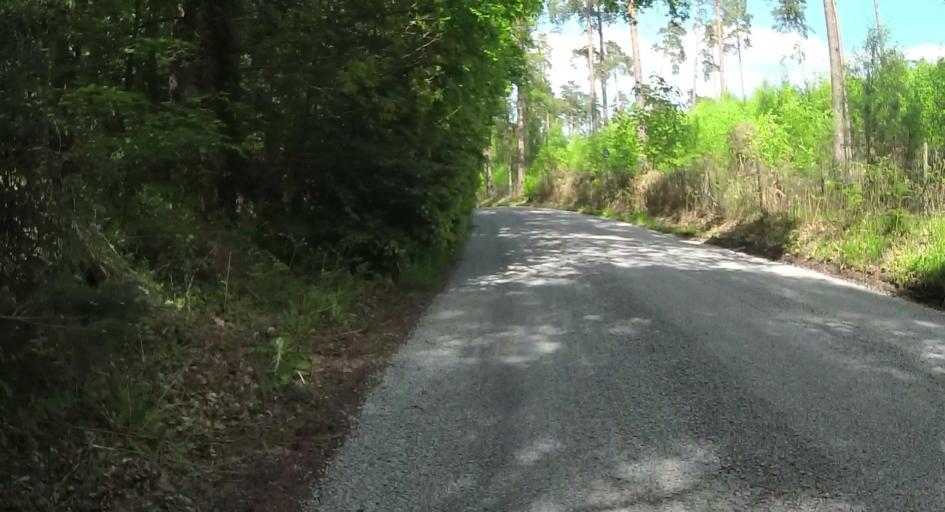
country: GB
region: England
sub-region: Surrey
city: Farnham
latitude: 51.1851
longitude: -0.8000
